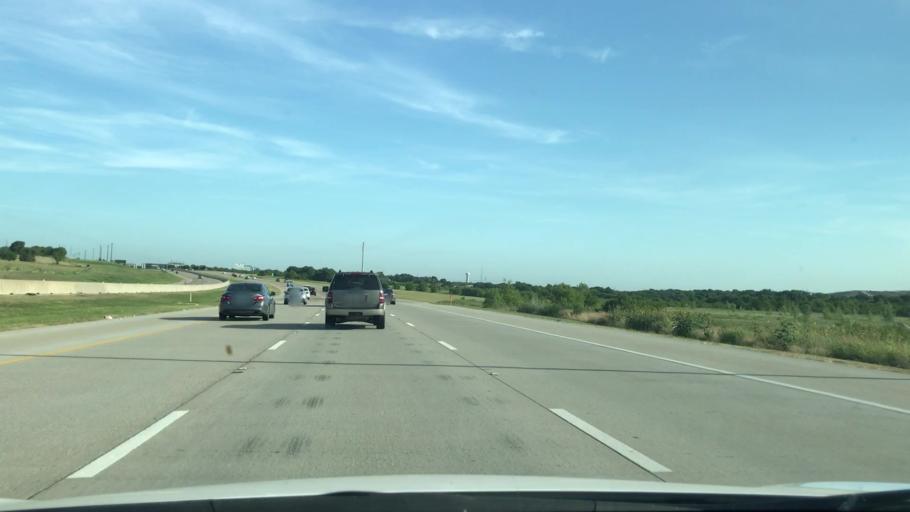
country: US
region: Texas
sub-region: Dallas County
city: Rowlett
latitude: 32.9367
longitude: -96.5533
